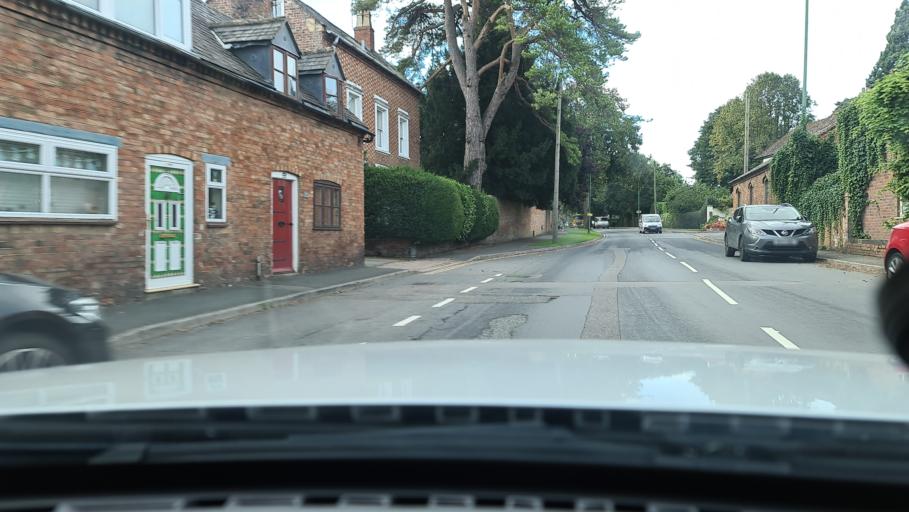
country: GB
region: England
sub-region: Warwickshire
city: Shipston on Stour
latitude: 52.0605
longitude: -1.6240
